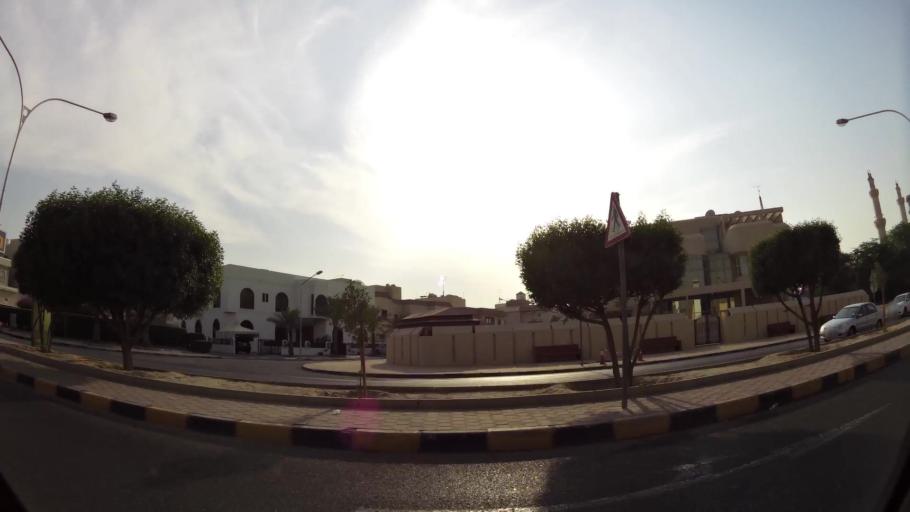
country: KW
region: Muhafazat Hawalli
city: Hawalli
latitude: 29.3122
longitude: 48.0063
